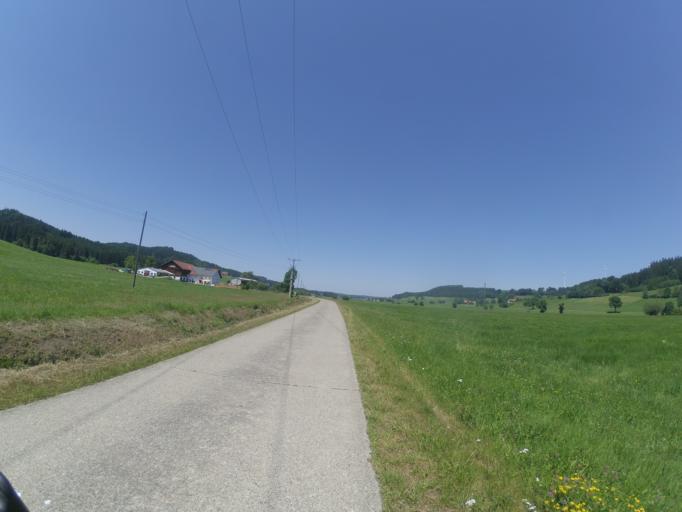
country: DE
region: Bavaria
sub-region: Swabia
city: Untrasried
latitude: 47.8621
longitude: 10.3499
